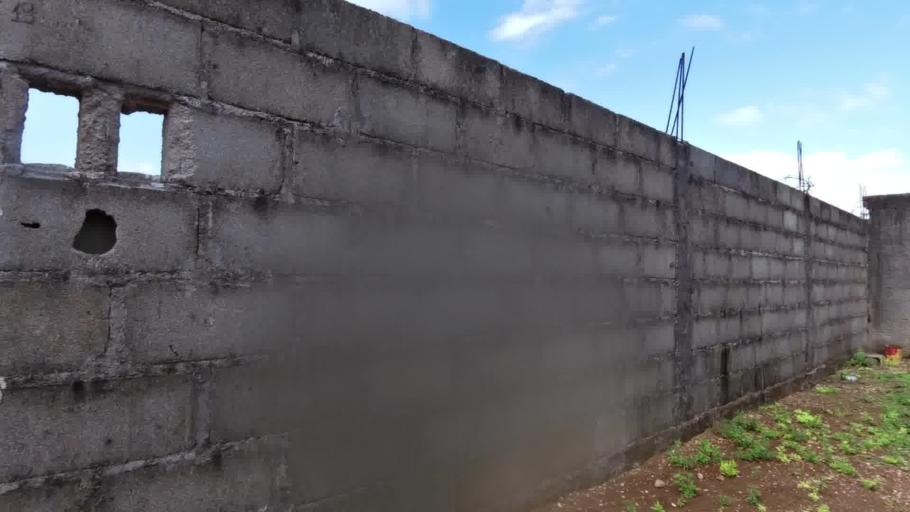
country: BR
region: Espirito Santo
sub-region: Piuma
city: Piuma
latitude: -20.8092
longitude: -40.6574
